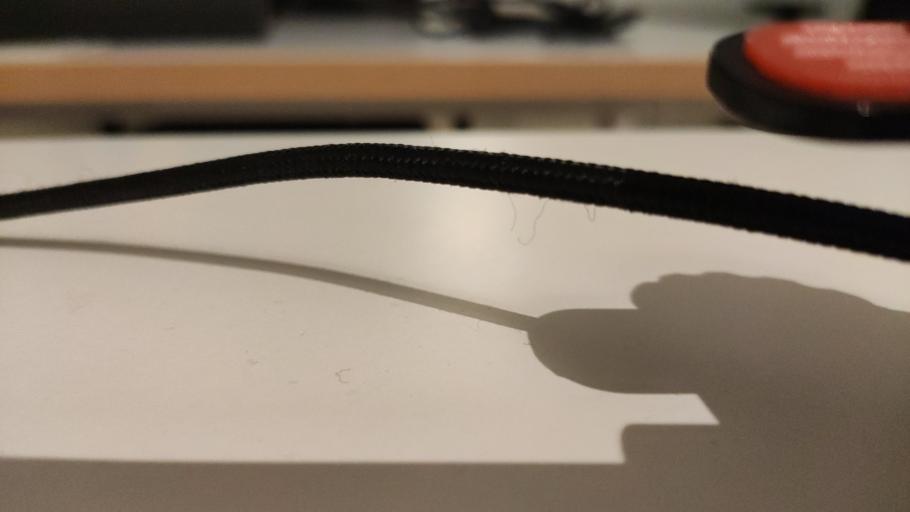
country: RU
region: Moskovskaya
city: Gorshkovo
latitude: 56.3719
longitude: 37.4216
